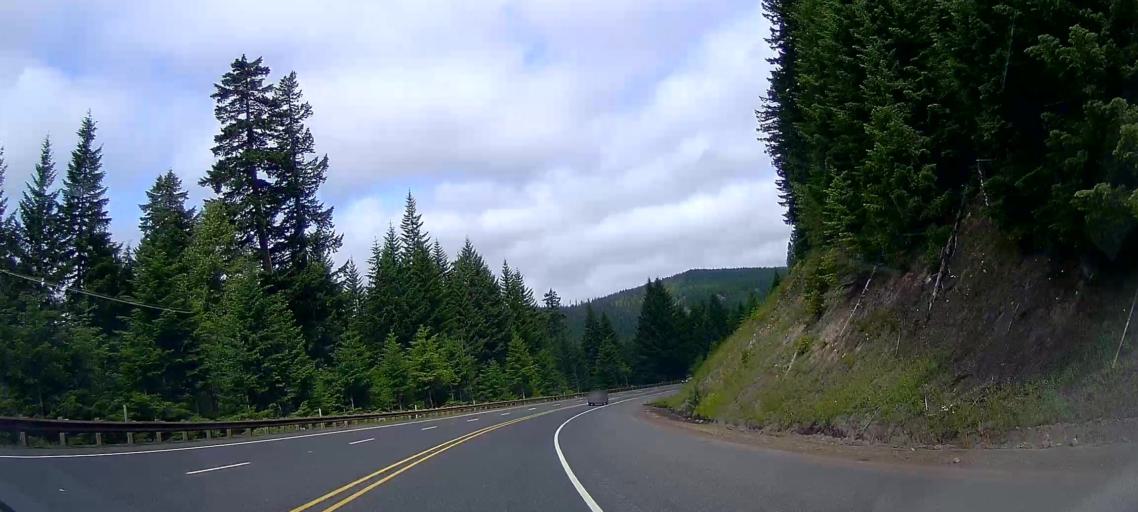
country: US
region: Oregon
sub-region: Clackamas County
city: Mount Hood Village
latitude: 45.2415
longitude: -121.7049
